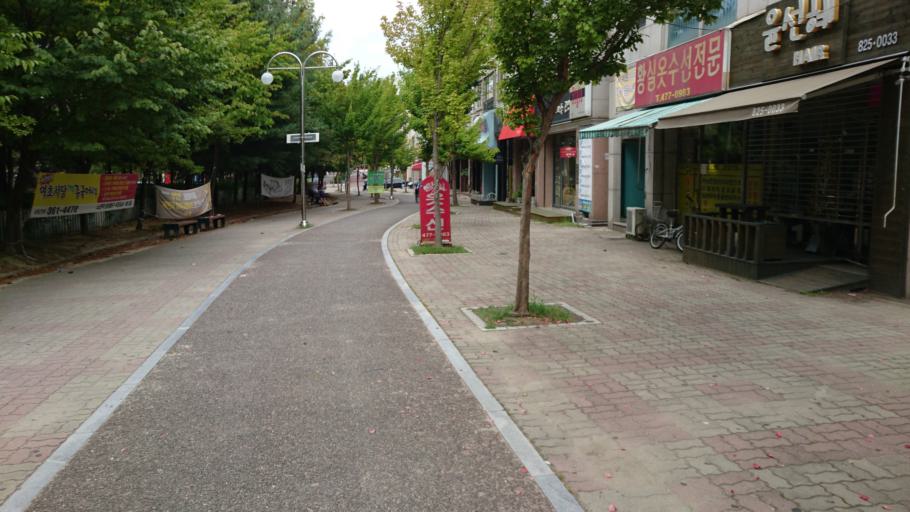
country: KR
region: Daejeon
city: Songgang-dong
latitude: 36.3740
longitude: 127.3216
